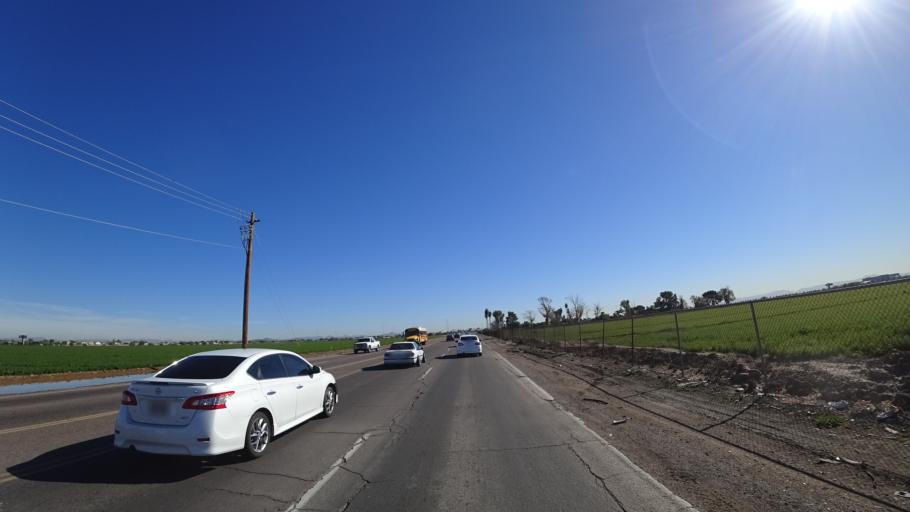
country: US
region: Arizona
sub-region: Maricopa County
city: Tolleson
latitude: 33.4937
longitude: -112.2717
